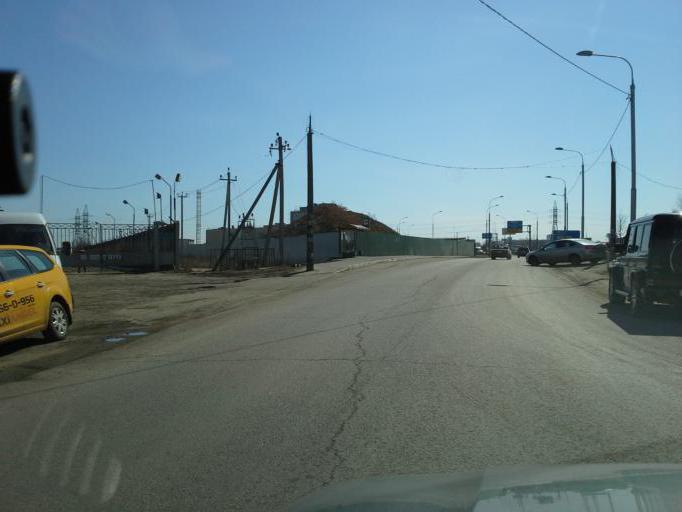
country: RU
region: Moskovskaya
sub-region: Leninskiy Rayon
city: Vnukovo
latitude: 55.6239
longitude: 37.2656
